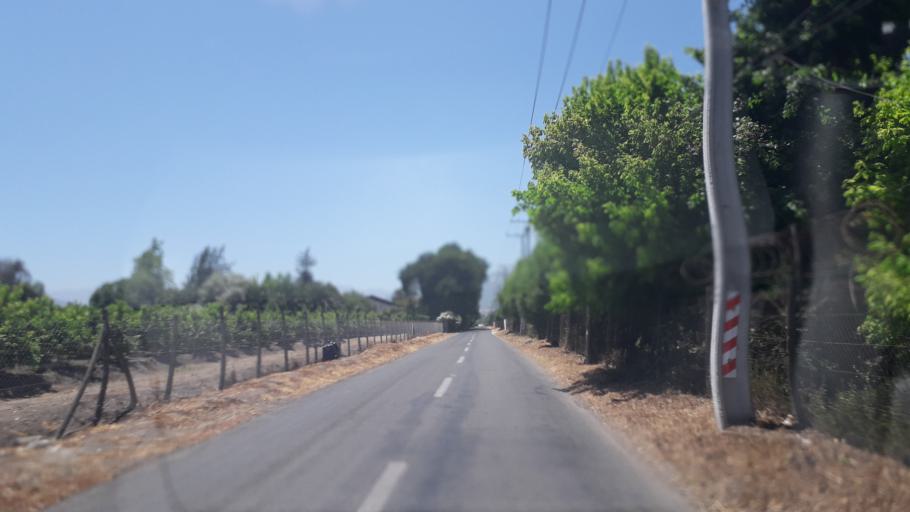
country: CL
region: Valparaiso
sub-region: Provincia de Quillota
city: Quillota
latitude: -32.9275
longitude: -71.2518
